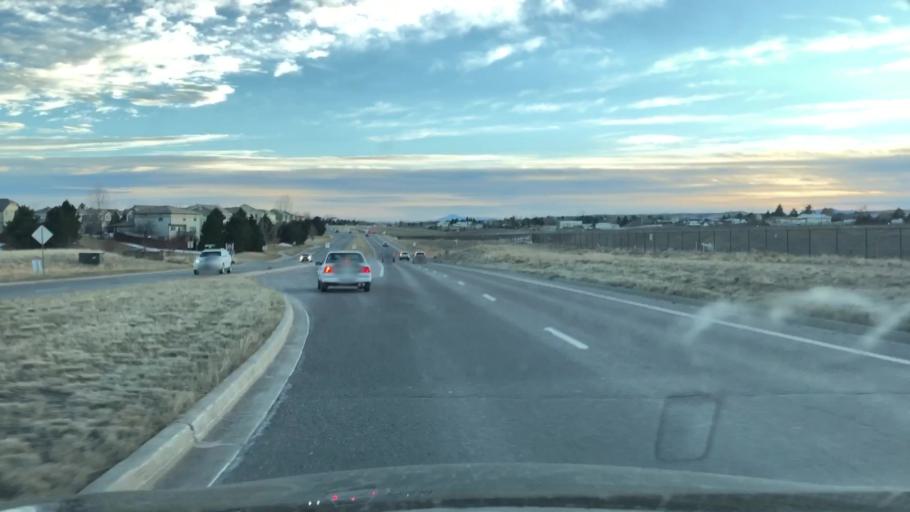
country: US
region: Colorado
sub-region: Douglas County
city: Stonegate
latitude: 39.5500
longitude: -104.8089
